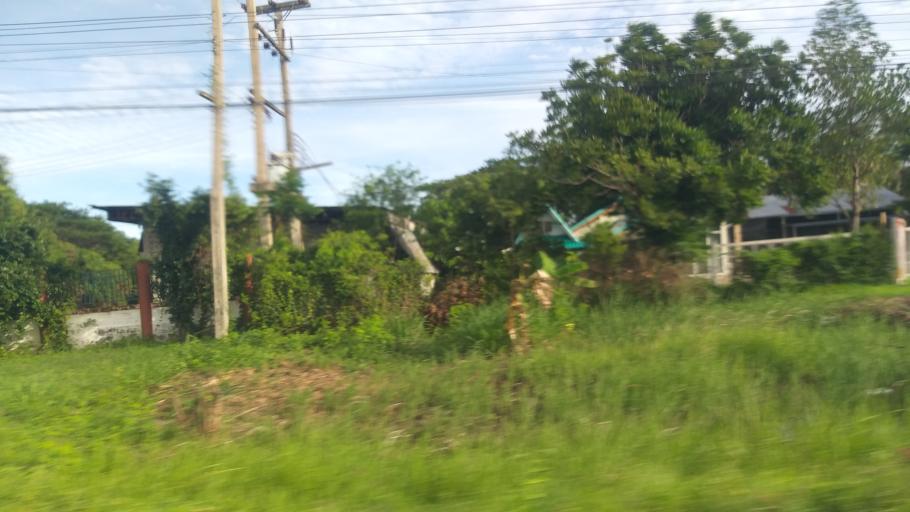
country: TH
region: Chaiyaphum
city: Ban Thaen
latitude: 16.3968
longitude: 102.3347
